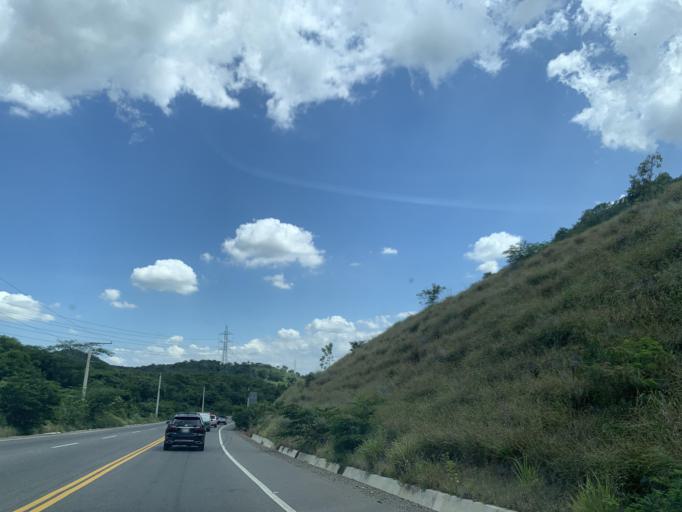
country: DO
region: Santiago
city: Villa Bisono
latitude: 19.6042
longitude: -70.8374
